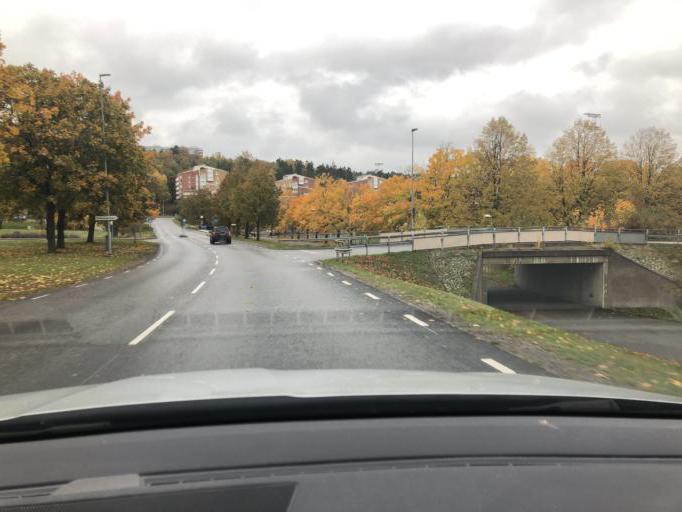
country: SE
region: Stockholm
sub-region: Botkyrka Kommun
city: Alby
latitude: 59.2362
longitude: 17.8518
